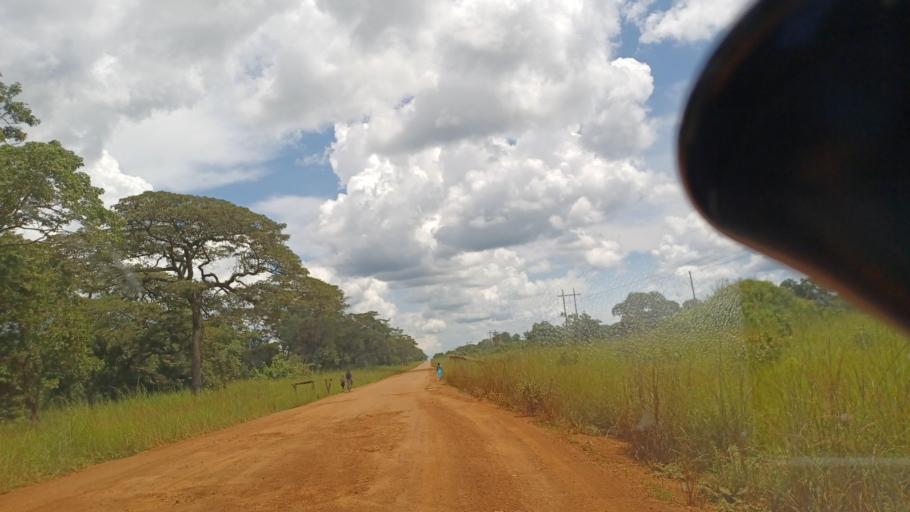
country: ZM
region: North-Western
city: Solwezi
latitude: -12.6980
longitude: 26.0383
